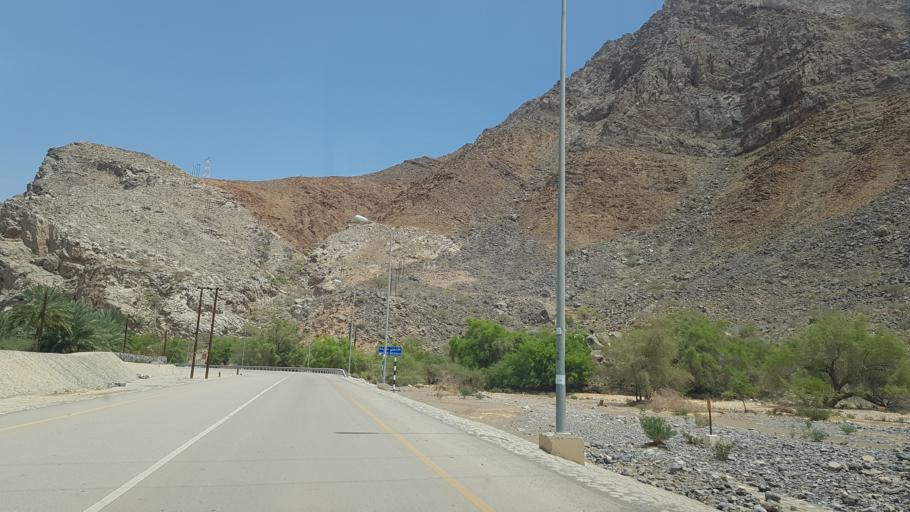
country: OM
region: Muhafazat ad Dakhiliyah
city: Izki
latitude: 22.9510
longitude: 57.6731
